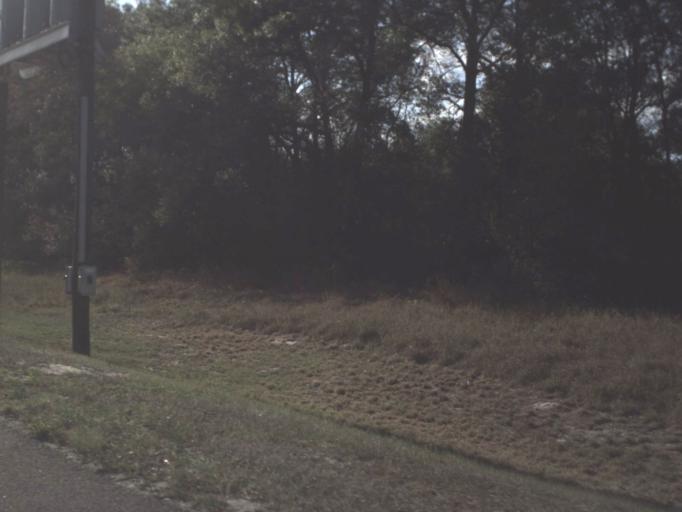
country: US
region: Florida
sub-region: Lake County
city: Mount Plymouth
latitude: 28.8127
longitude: -81.5206
